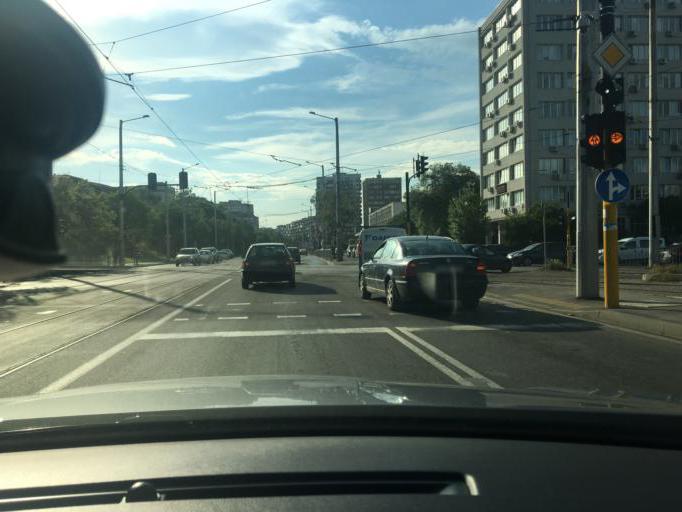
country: BG
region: Sofia-Capital
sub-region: Stolichna Obshtina
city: Sofia
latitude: 42.6768
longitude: 23.3697
